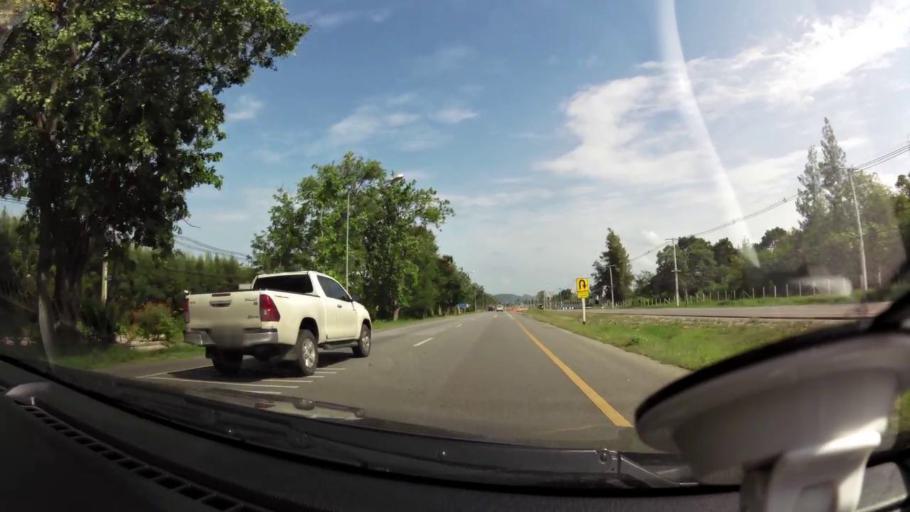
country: TH
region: Prachuap Khiri Khan
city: Hua Hin
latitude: 12.5091
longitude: 99.9671
